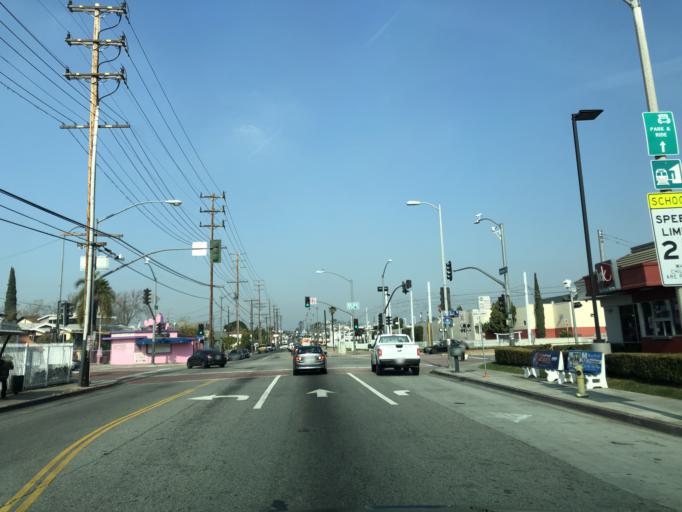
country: US
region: California
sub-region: Los Angeles County
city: Boyle Heights
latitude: 34.0327
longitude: -118.1924
